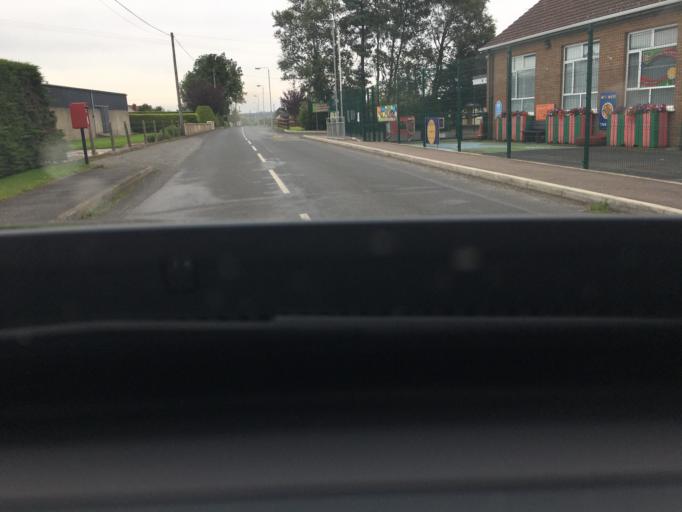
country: GB
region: Northern Ireland
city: Coalisland
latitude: 54.5390
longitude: -6.6224
